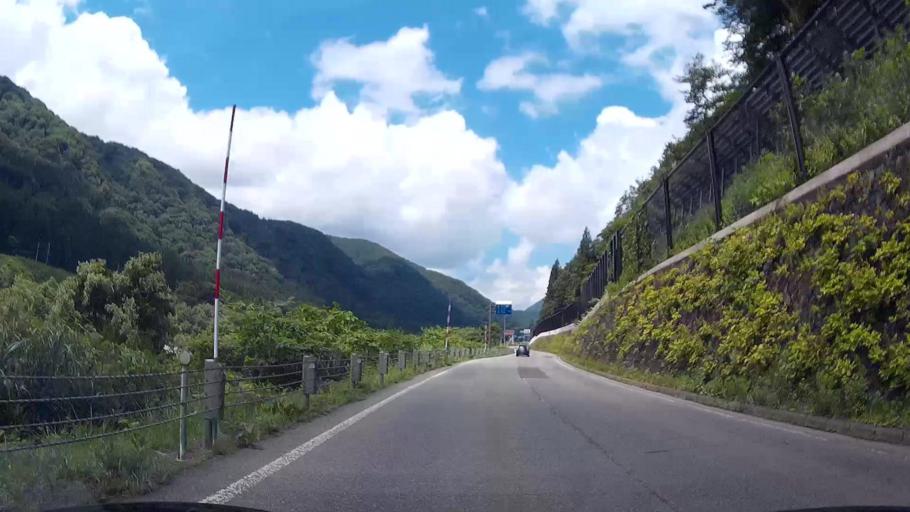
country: JP
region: Niigata
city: Shiozawa
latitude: 36.8883
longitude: 138.7758
